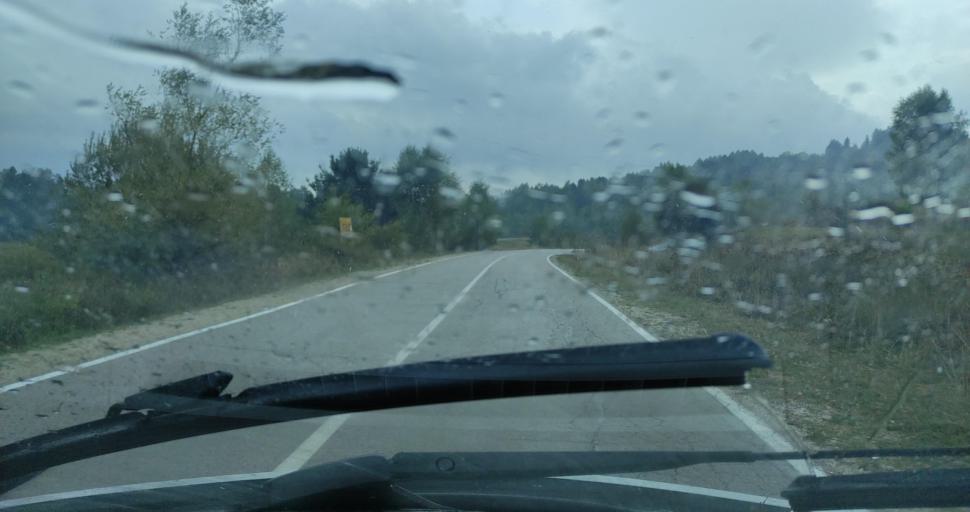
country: RS
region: Central Serbia
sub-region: Jablanicki Okrug
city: Crna Trava
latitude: 42.7357
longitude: 22.3311
